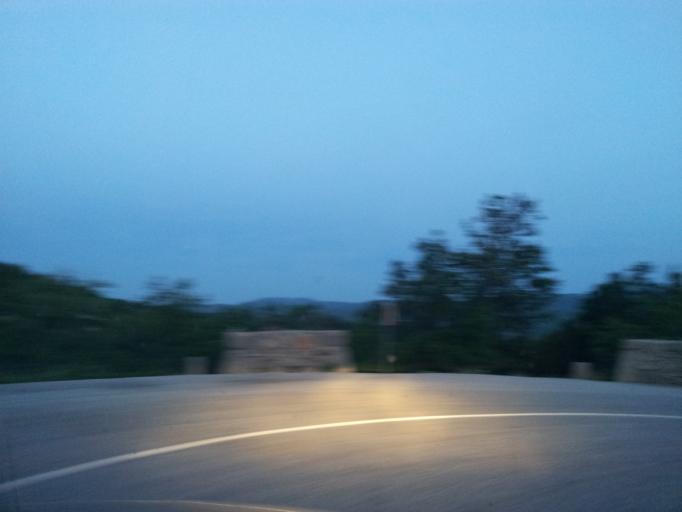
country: HR
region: Zadarska
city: Obrovac
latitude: 44.2269
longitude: 15.6749
